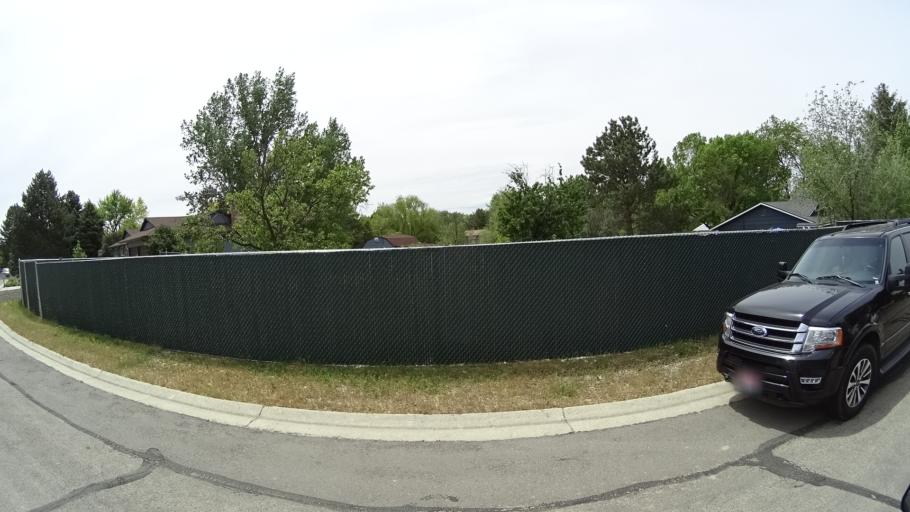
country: US
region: Idaho
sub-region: Ada County
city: Meridian
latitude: 43.5567
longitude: -116.3266
